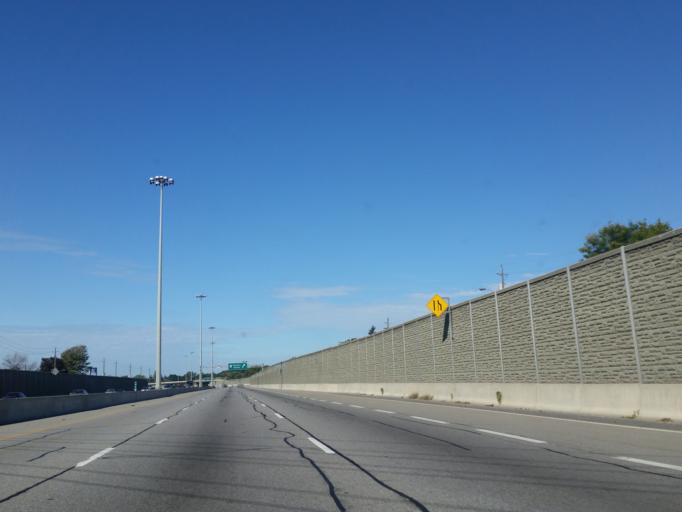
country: CA
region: Ontario
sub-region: Regional Municipality of Niagara
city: St. Catharines
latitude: 43.1785
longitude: -79.2578
